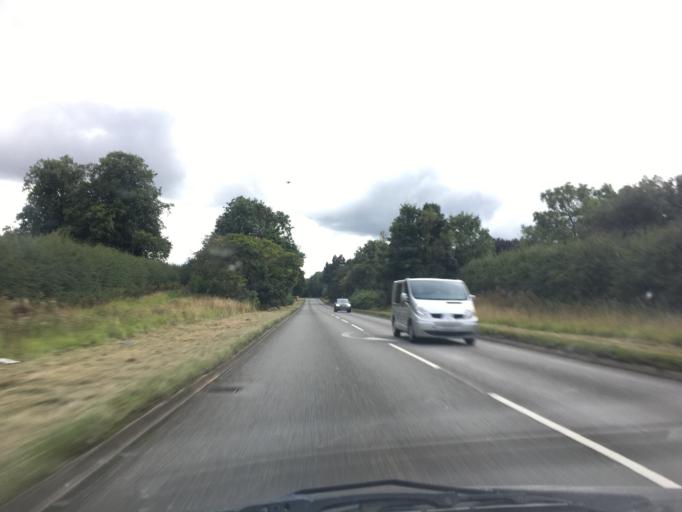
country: GB
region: England
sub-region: Leicestershire
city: Lutterworth
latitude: 52.4365
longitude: -1.2062
